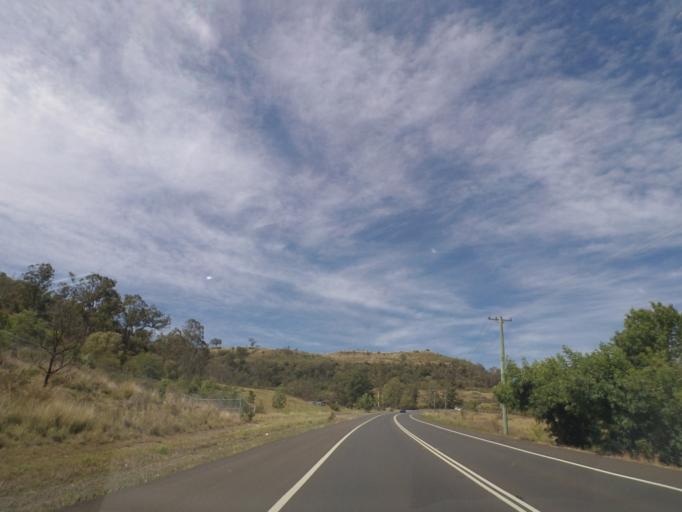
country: AU
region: New South Wales
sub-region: Wollondilly
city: Picton
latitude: -34.1610
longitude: 150.6419
